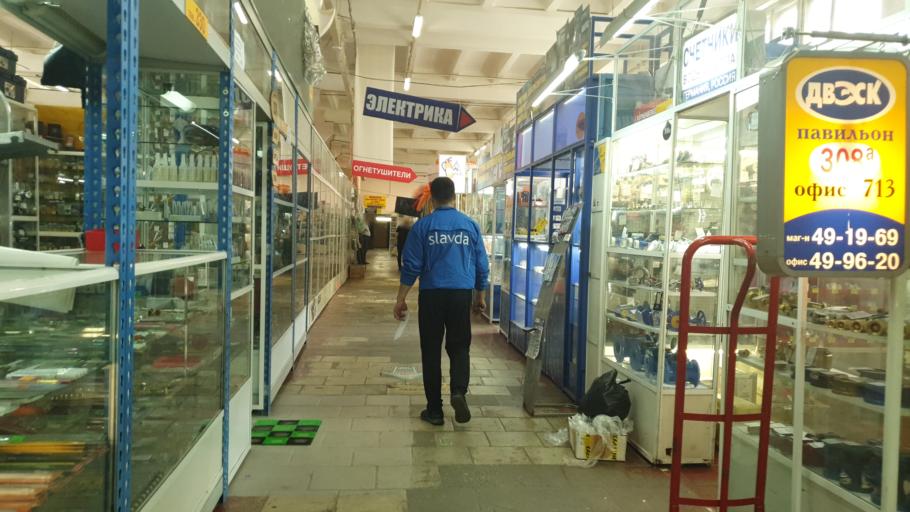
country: RU
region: Primorskiy
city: Vladivostok
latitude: 43.1116
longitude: 131.9149
